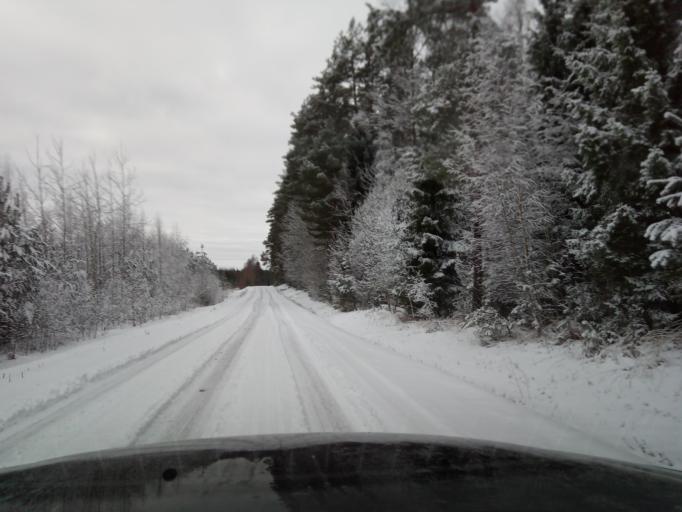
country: LT
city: Zarasai
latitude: 55.6802
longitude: 26.0037
